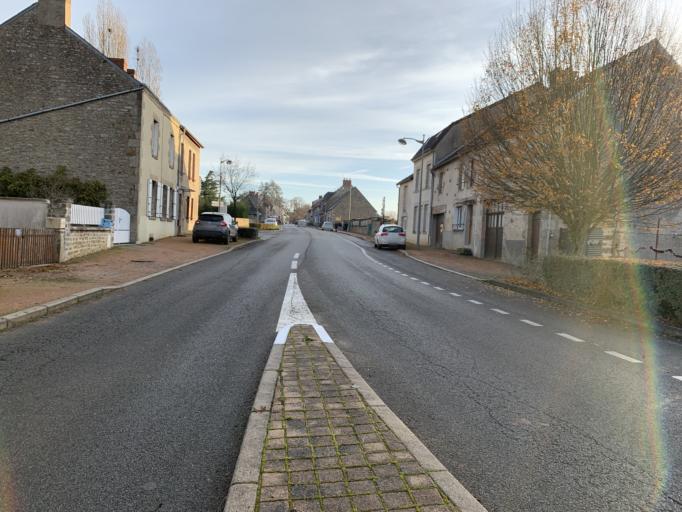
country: FR
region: Limousin
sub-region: Departement de la Creuse
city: Ajain
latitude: 46.2068
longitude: 1.9956
